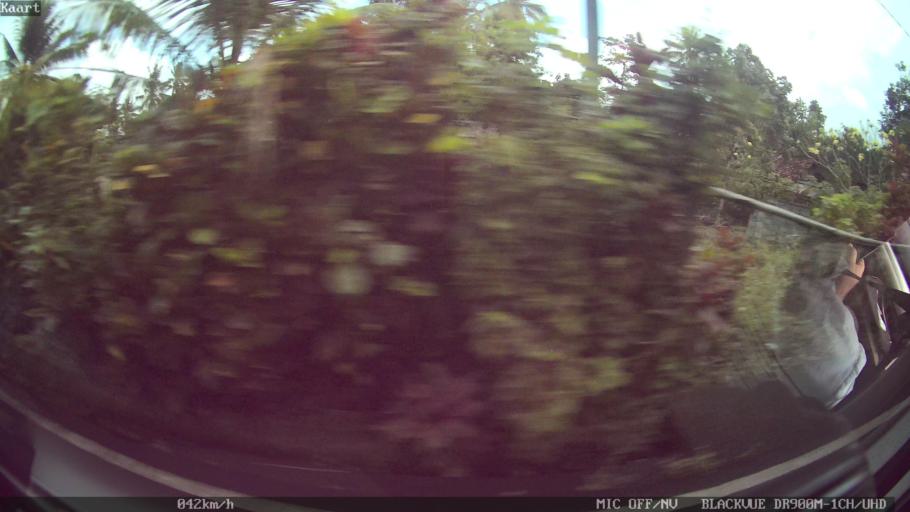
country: ID
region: Bali
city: Banjar Mambalkajanan
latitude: -8.5572
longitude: 115.2087
